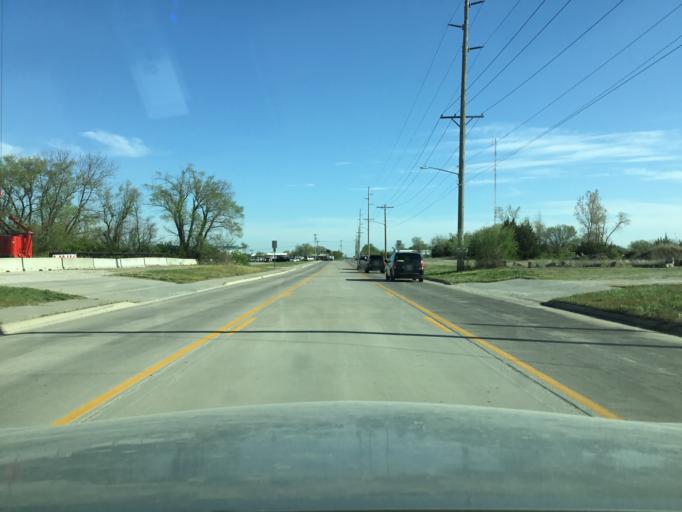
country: US
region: Kansas
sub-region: Neosho County
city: Chanute
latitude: 37.6861
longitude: -95.4710
